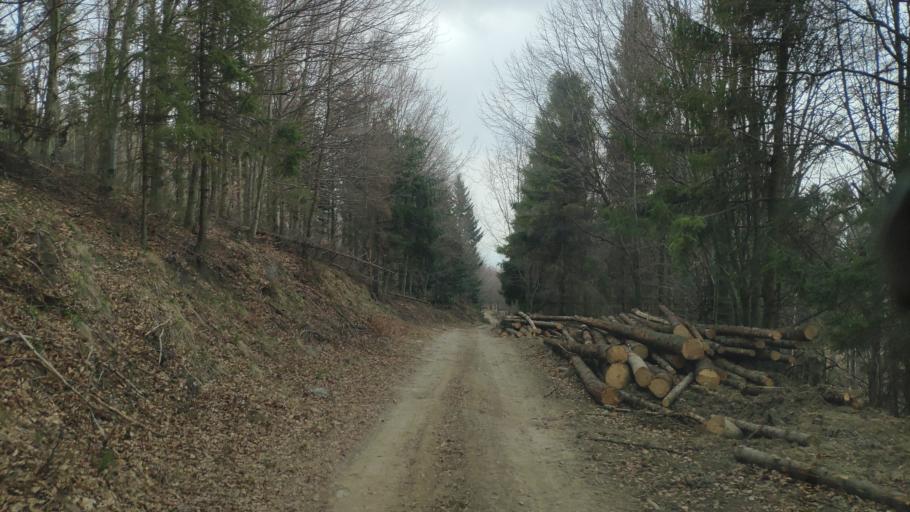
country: SK
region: Kosicky
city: Moldava nad Bodvou
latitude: 48.7474
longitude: 21.0400
